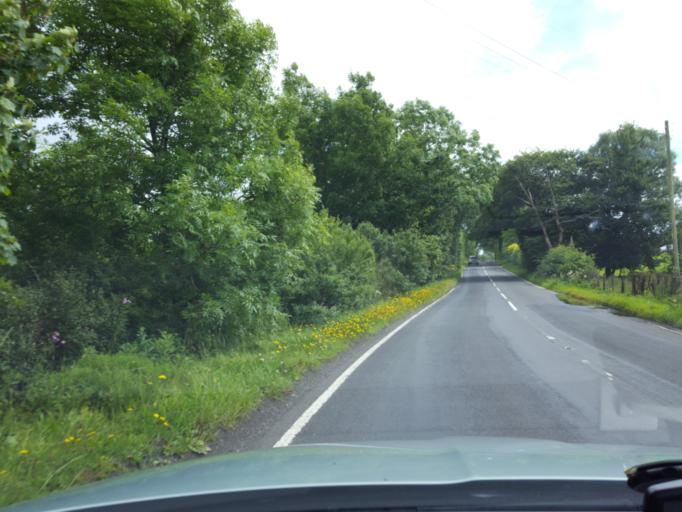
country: GB
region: Scotland
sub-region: West Lothian
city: Bathgate
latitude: 55.9167
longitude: -3.6690
